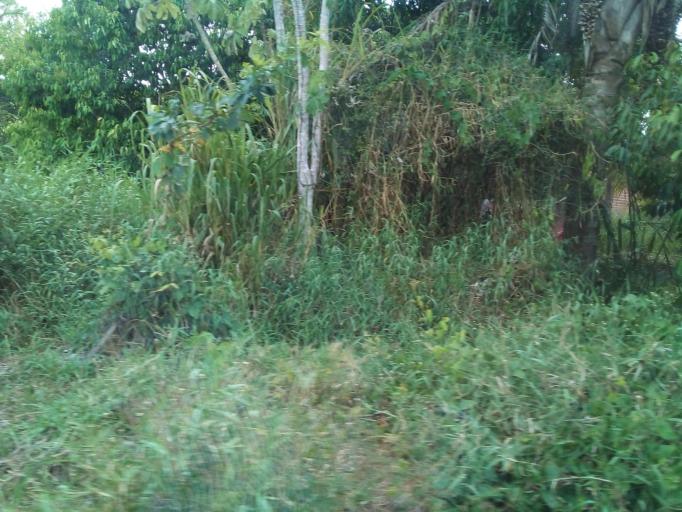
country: BR
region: Maranhao
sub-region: Itapecuru Mirim
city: Itapecuru Mirim
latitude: -3.1318
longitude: -44.3328
